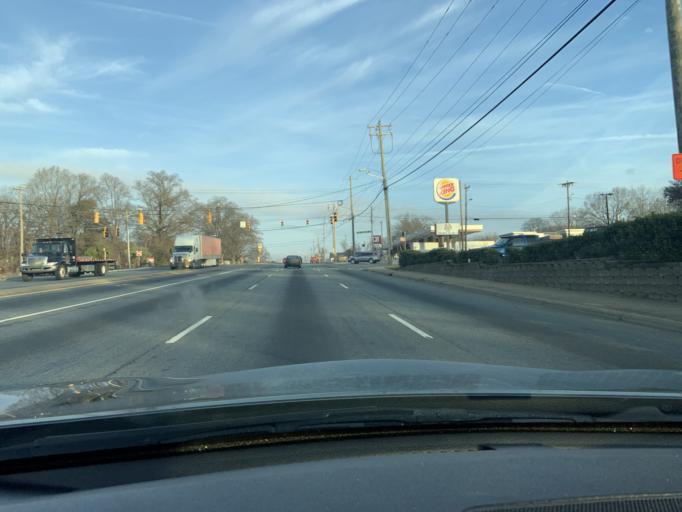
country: US
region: North Carolina
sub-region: Mecklenburg County
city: Charlotte
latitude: 35.2661
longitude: -80.8816
